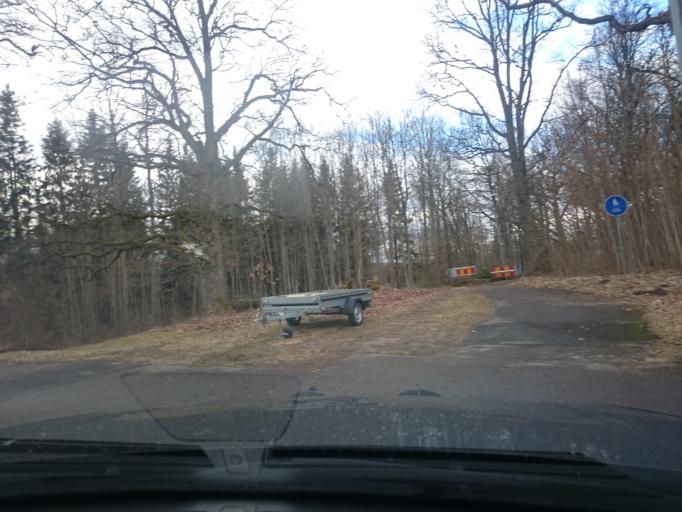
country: SE
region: Joenkoeping
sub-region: Vetlanda Kommun
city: Vetlanda
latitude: 57.3035
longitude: 15.1234
